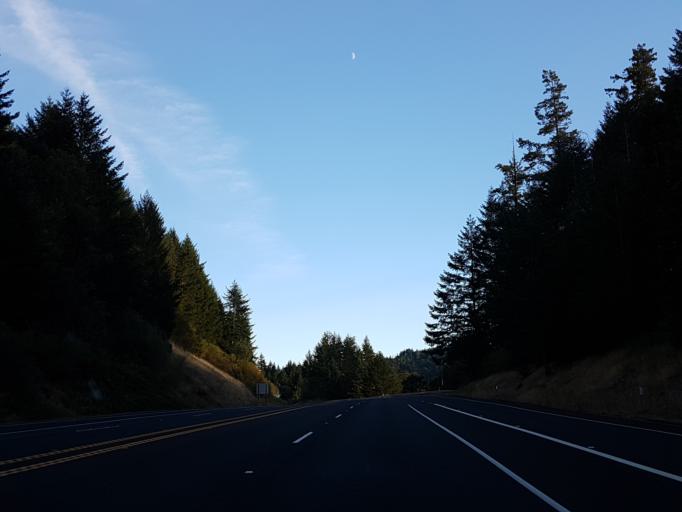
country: US
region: California
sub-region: Humboldt County
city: Redway
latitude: 39.9421
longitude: -123.7785
